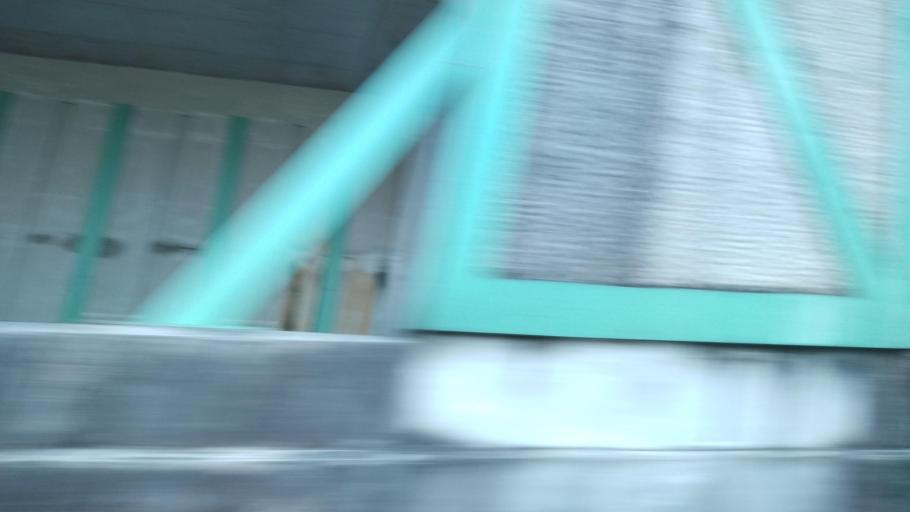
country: TW
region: Taipei
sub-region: Taipei
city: Banqiao
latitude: 24.9589
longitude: 121.5151
